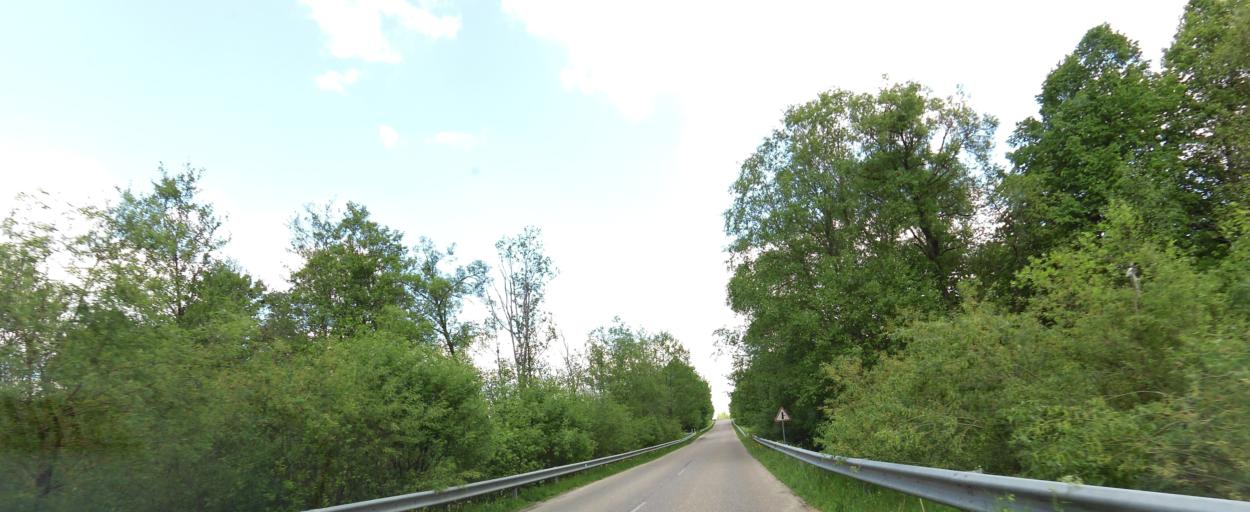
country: LT
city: Trakai
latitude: 54.6797
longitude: 24.9526
